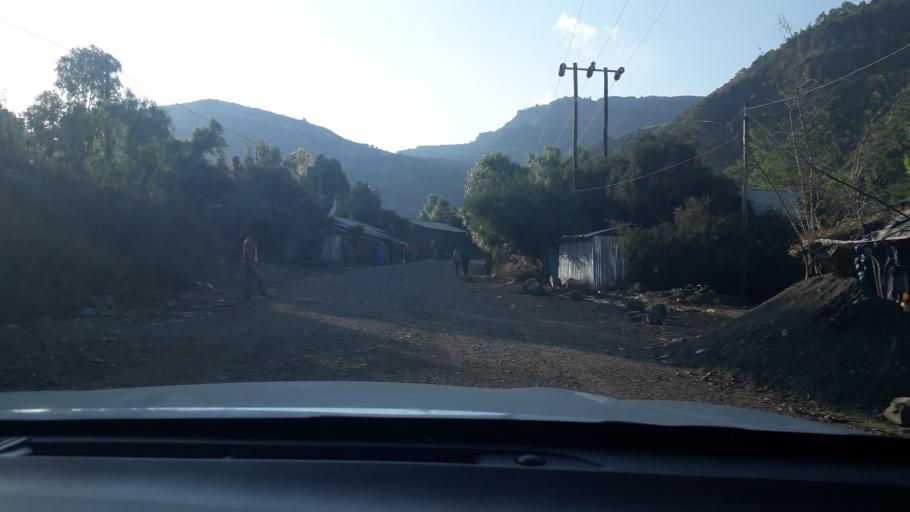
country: ET
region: Amhara
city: Lalibela
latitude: 11.5374
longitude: 39.2458
